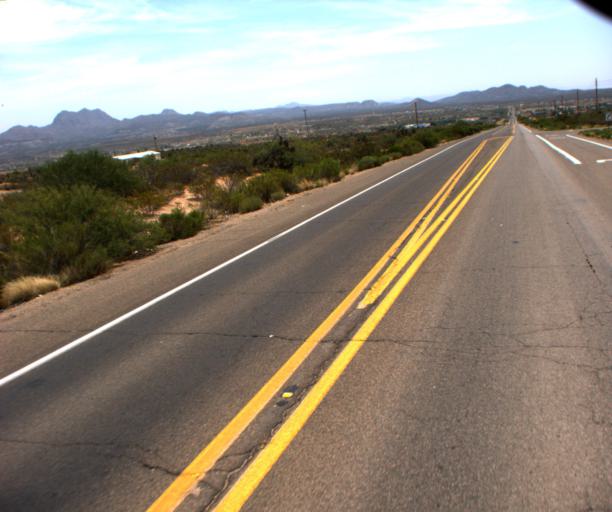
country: US
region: Arizona
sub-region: Gila County
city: Peridot
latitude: 33.3031
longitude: -110.4770
